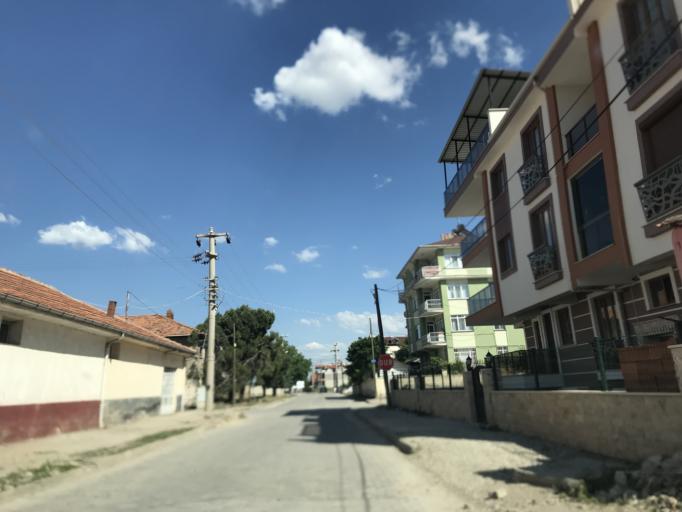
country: TR
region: Denizli
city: Civril
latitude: 38.3031
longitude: 29.7443
